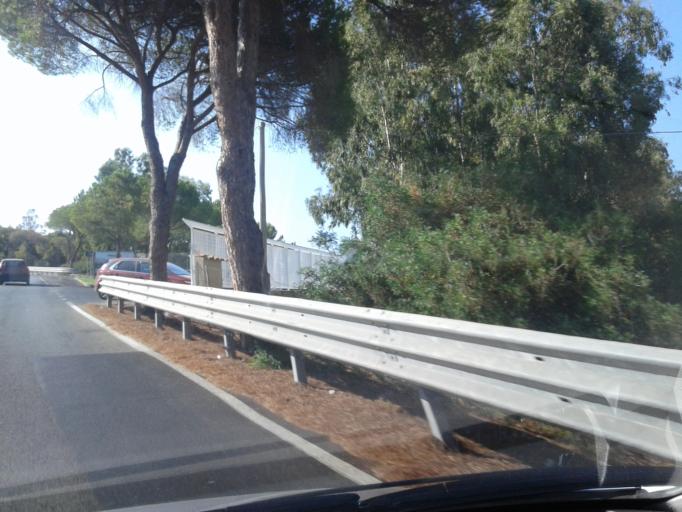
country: IT
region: Sicily
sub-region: Palermo
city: Finale
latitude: 38.0242
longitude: 14.1490
